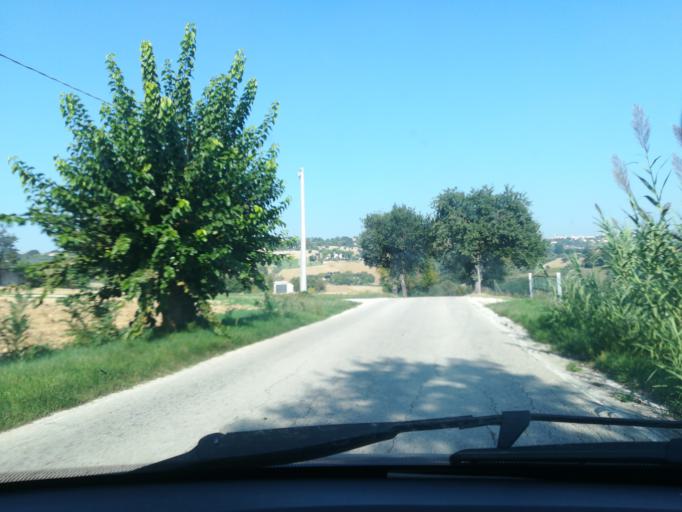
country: IT
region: The Marches
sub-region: Provincia di Macerata
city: Macerata
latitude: 43.2701
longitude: 13.4509
